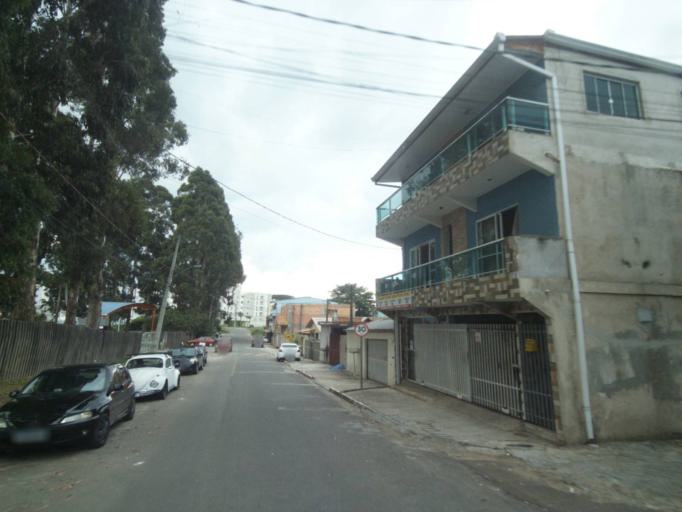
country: BR
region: Parana
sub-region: Curitiba
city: Curitiba
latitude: -25.4430
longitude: -49.3568
